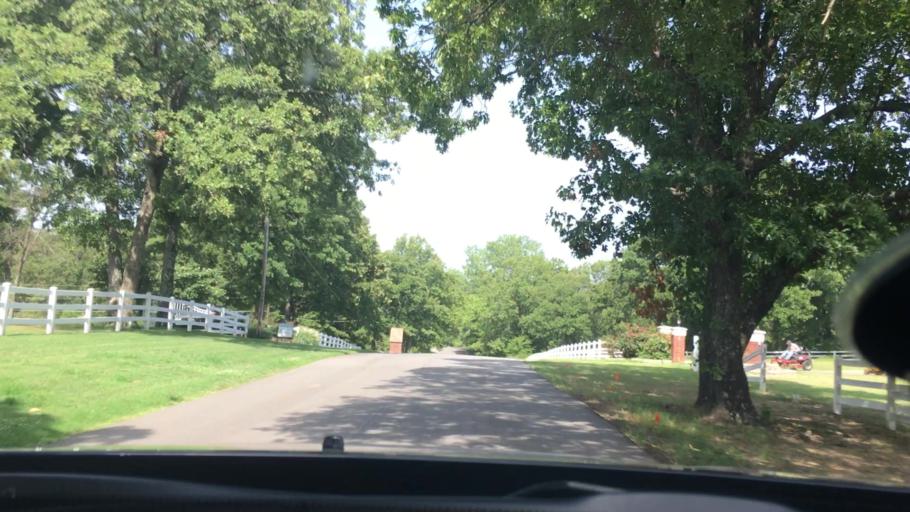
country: US
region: Oklahoma
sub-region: Atoka County
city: Atoka
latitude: 34.3603
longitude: -96.1553
